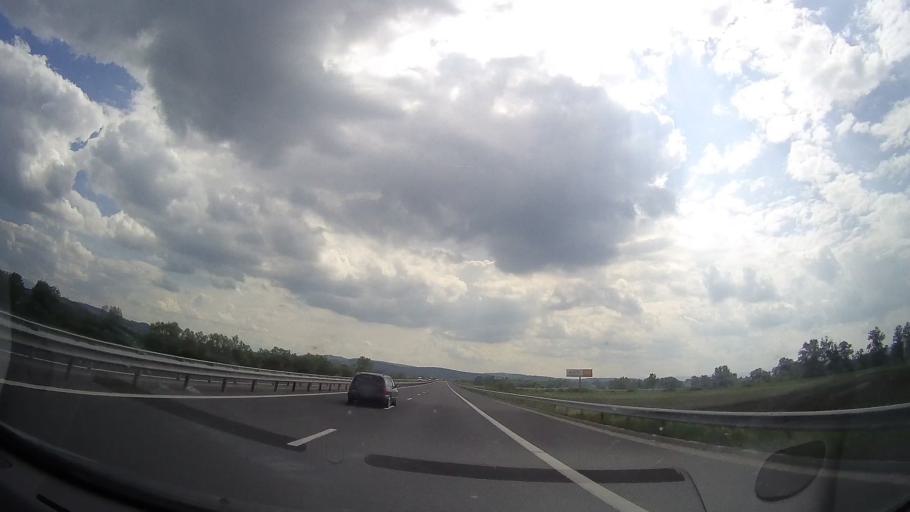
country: RO
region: Hunedoara
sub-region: Comuna Turdas
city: Pricaz
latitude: 45.8649
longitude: 23.1538
